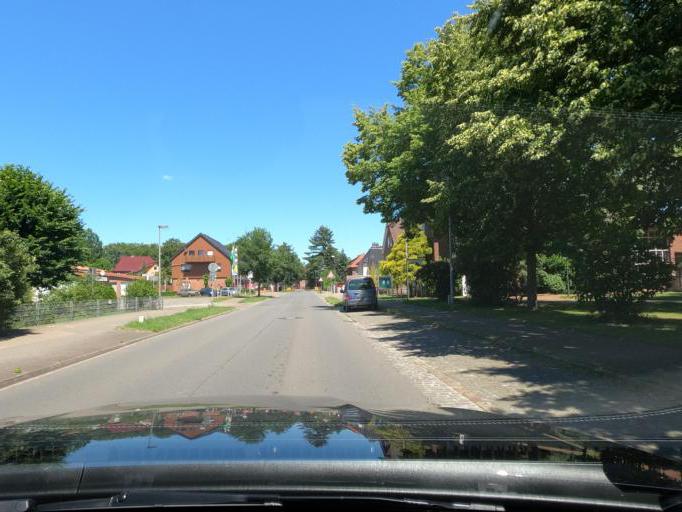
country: DE
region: Lower Saxony
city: Wathlingen
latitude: 52.5371
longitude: 10.1461
